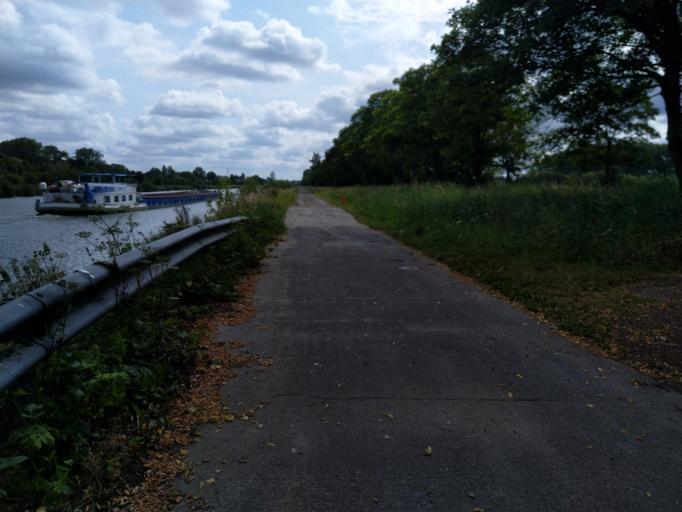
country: BE
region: Wallonia
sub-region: Province du Hainaut
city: Boussu
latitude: 50.4753
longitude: 3.7520
